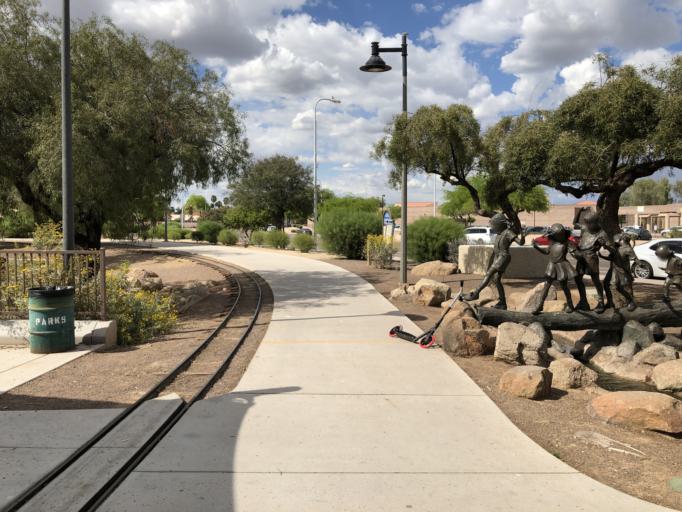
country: US
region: Arizona
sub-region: Maricopa County
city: Guadalupe
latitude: 33.3138
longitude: -111.9191
